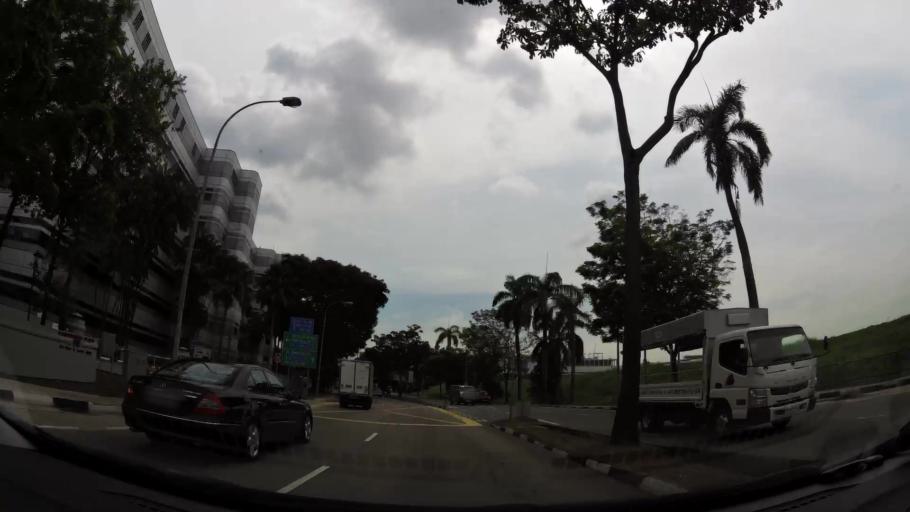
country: SG
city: Singapore
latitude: 1.3257
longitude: 103.7192
